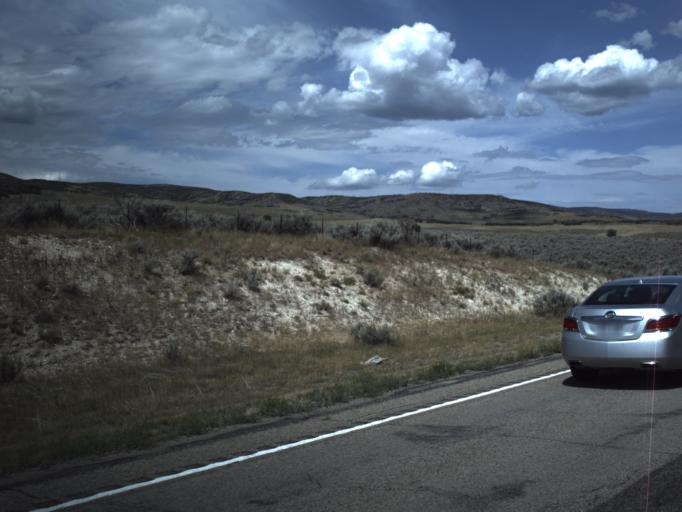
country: US
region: Utah
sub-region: Sanpete County
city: Fairview
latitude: 39.6953
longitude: -111.4624
